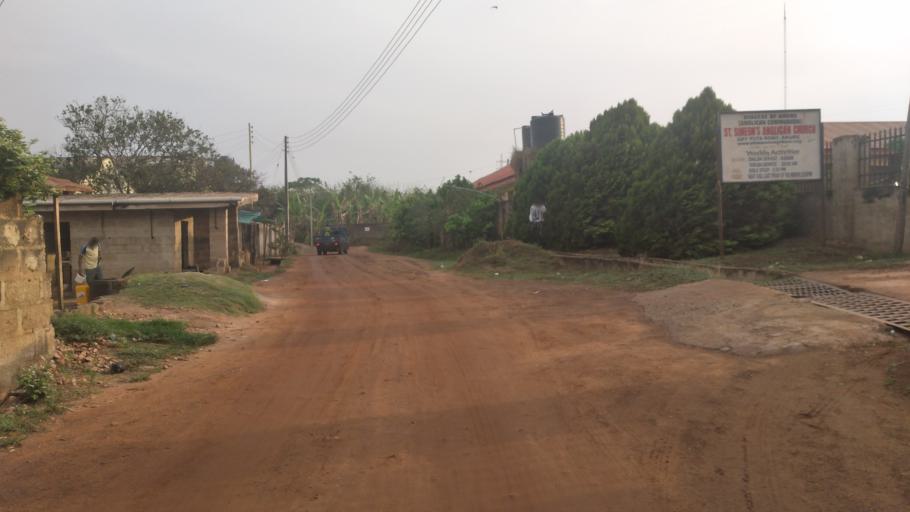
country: NG
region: Ondo
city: Akure
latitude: 7.2954
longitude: 5.1540
